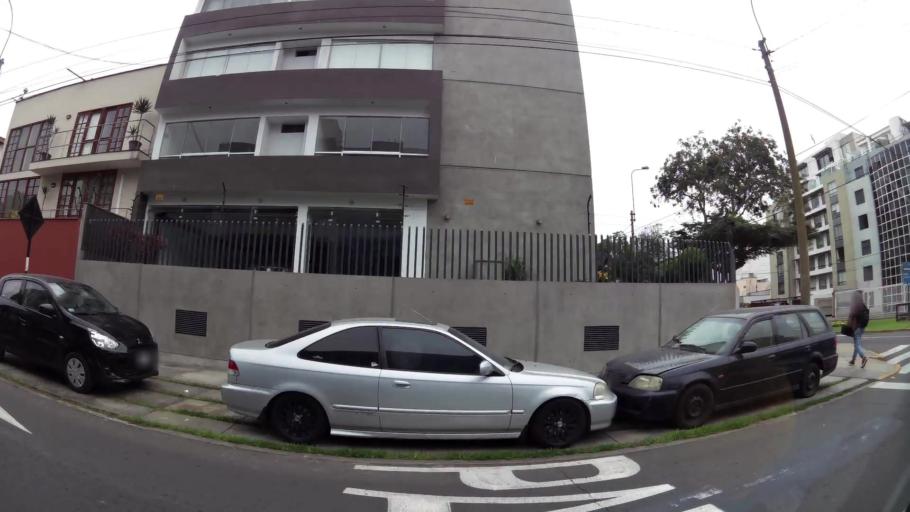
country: PE
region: Lima
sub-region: Lima
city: Surco
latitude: -12.1213
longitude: -77.0199
